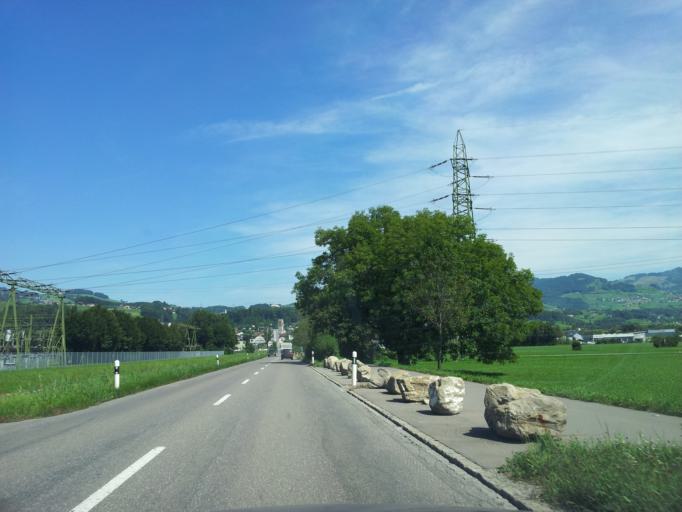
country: CH
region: Saint Gallen
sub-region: Wahlkreis See-Gaster
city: Uznach
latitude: 47.2192
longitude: 8.9745
